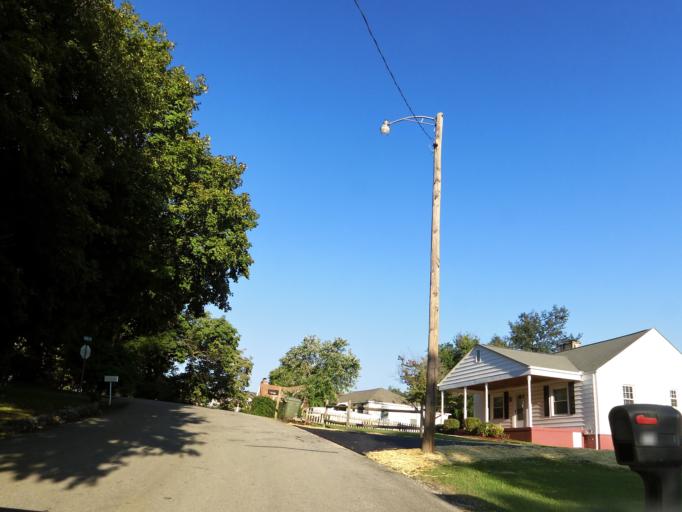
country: US
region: Tennessee
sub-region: Blount County
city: Eagleton Village
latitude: 35.7825
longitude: -83.9509
